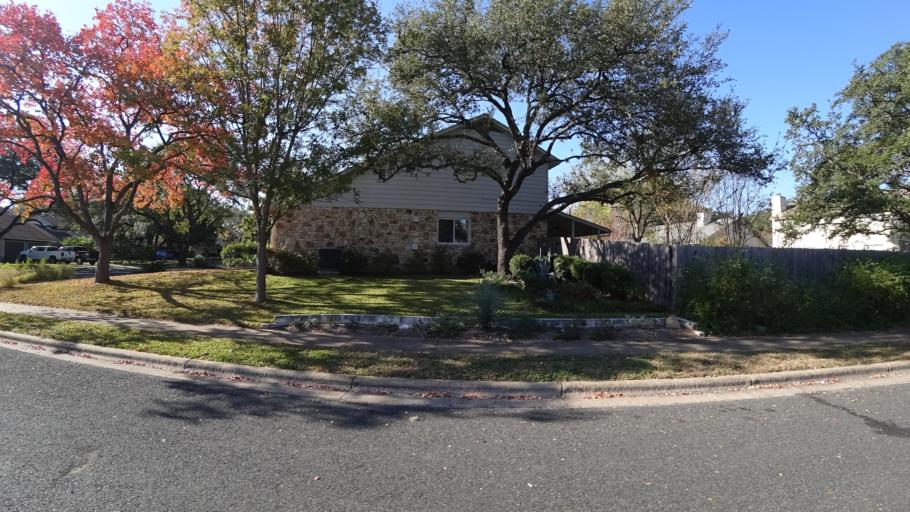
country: US
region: Texas
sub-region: Travis County
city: Shady Hollow
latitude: 30.2251
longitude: -97.8363
